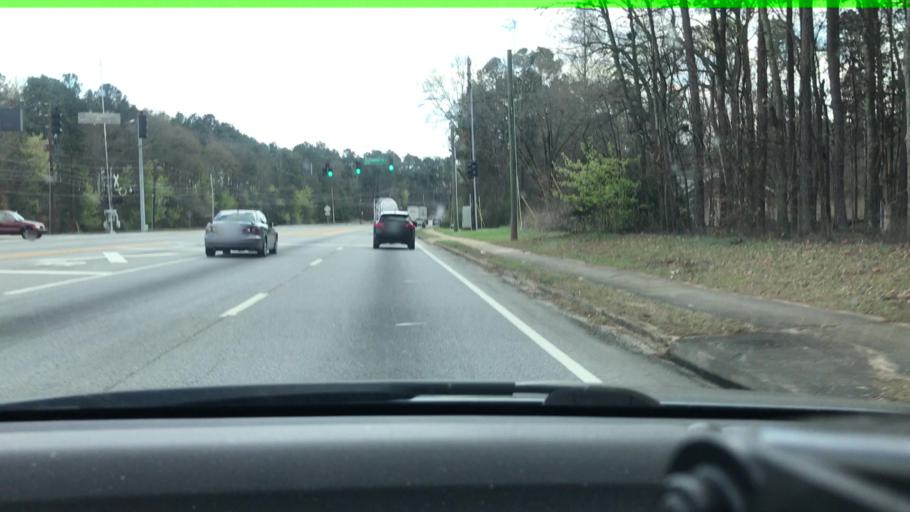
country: US
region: Georgia
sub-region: Clarke County
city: Country Club Estates
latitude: 33.9831
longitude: -83.4173
